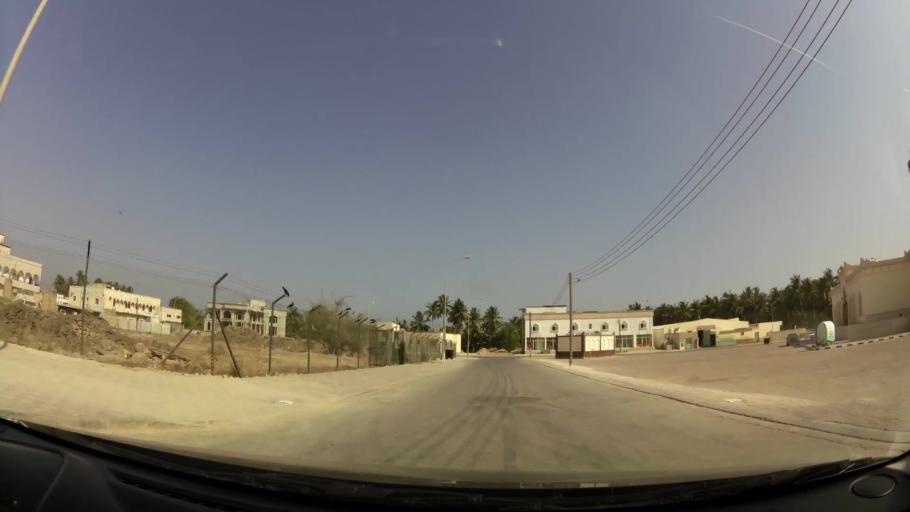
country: OM
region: Zufar
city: Salalah
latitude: 17.0017
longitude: 54.0414
